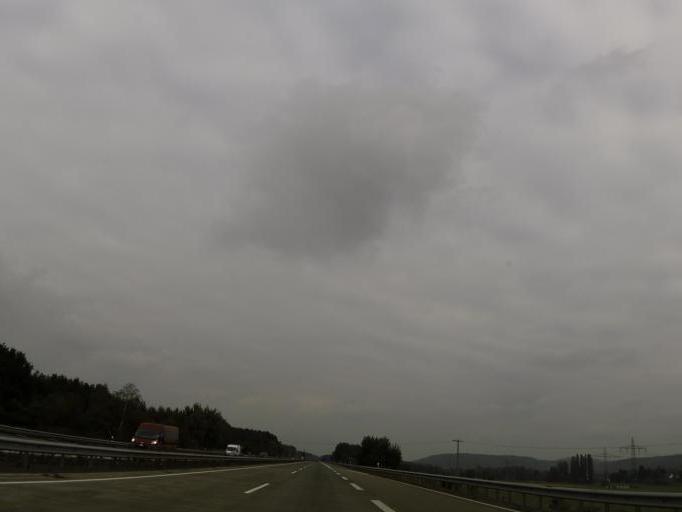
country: DE
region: Rheinland-Pfalz
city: Bruchmuhlbach-Miesau
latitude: 49.3822
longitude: 7.4238
